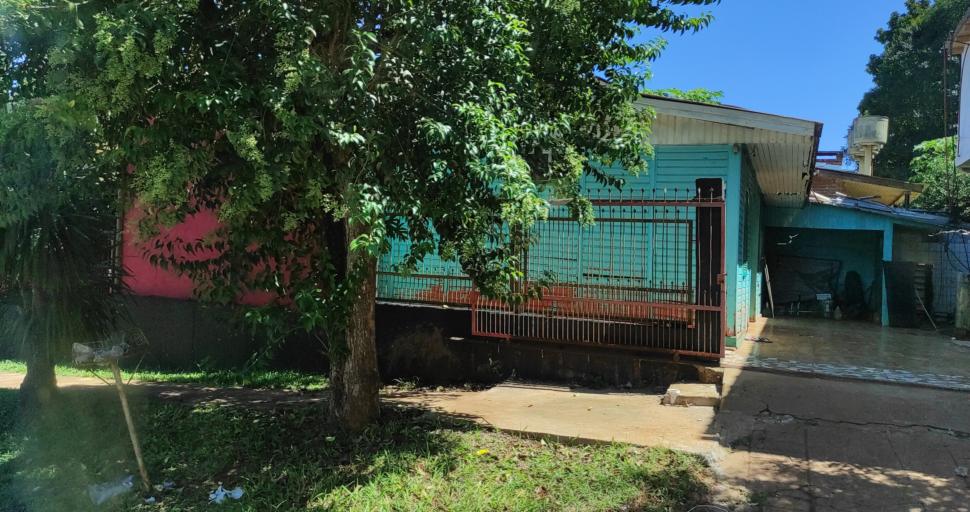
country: AR
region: Misiones
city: El Soberbio
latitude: -27.2947
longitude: -54.2017
